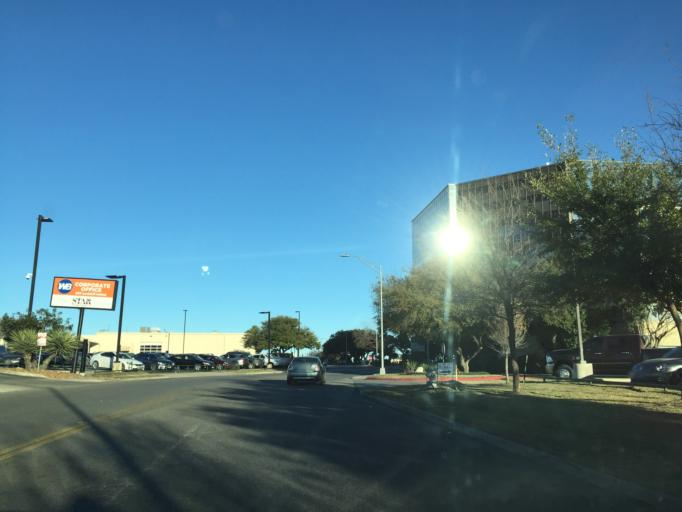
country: US
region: Texas
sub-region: Bexar County
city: Castle Hills
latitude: 29.5229
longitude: -98.5033
